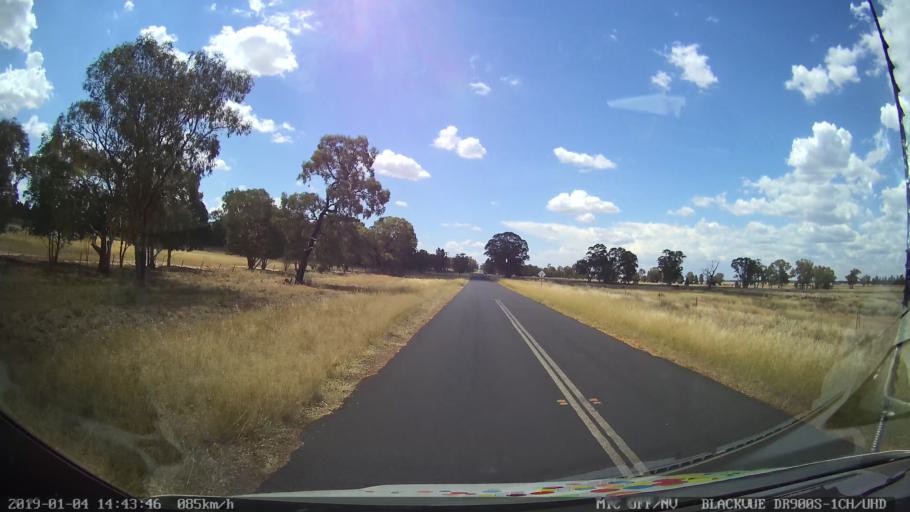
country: AU
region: New South Wales
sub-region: Dubbo Municipality
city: Dubbo
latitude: -32.1149
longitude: 148.6541
